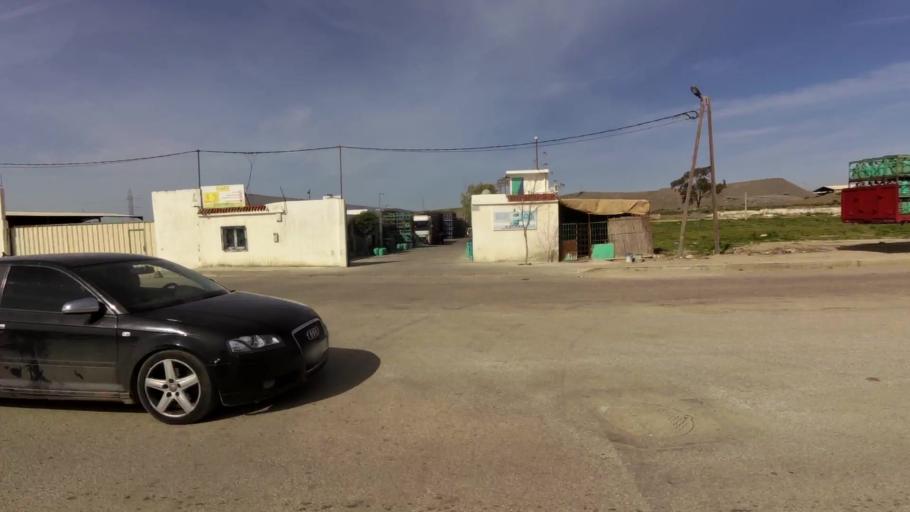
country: MA
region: Tanger-Tetouan
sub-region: Tanger-Assilah
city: Tangier
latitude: 35.7056
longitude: -5.8052
